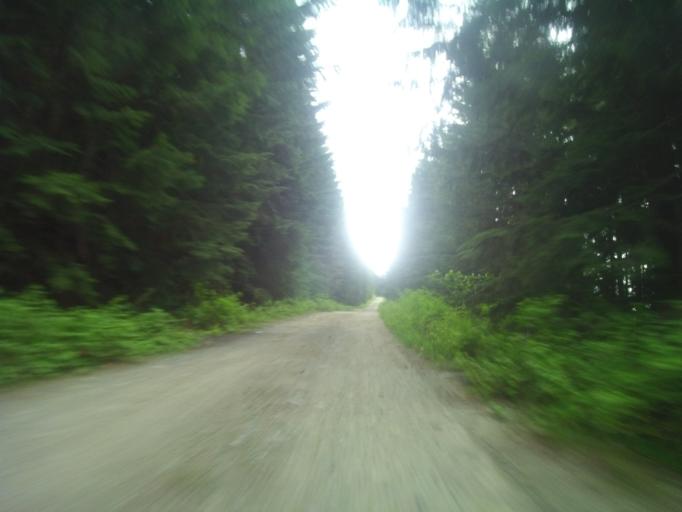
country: CA
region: British Columbia
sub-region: Fraser Valley Regional District
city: North Vancouver
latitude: 49.3731
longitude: -123.0623
